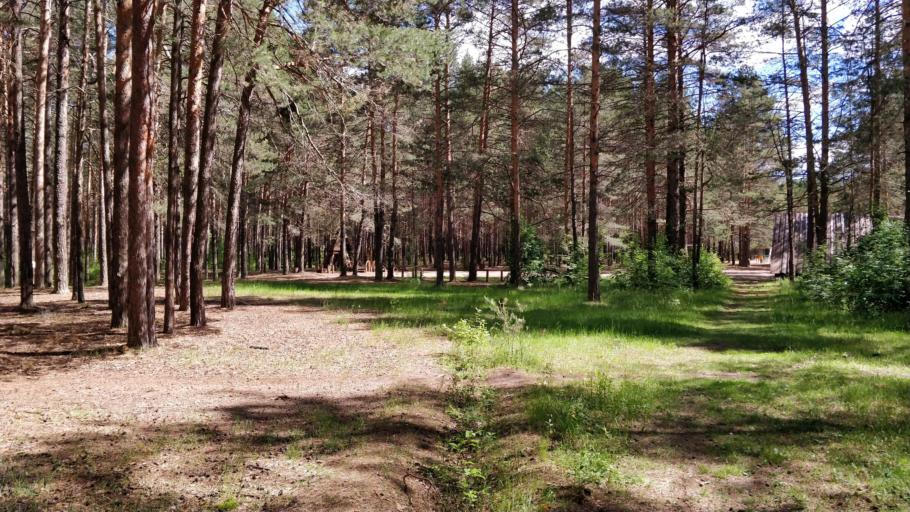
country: RU
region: Perm
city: Perm
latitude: 58.0595
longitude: 56.2894
